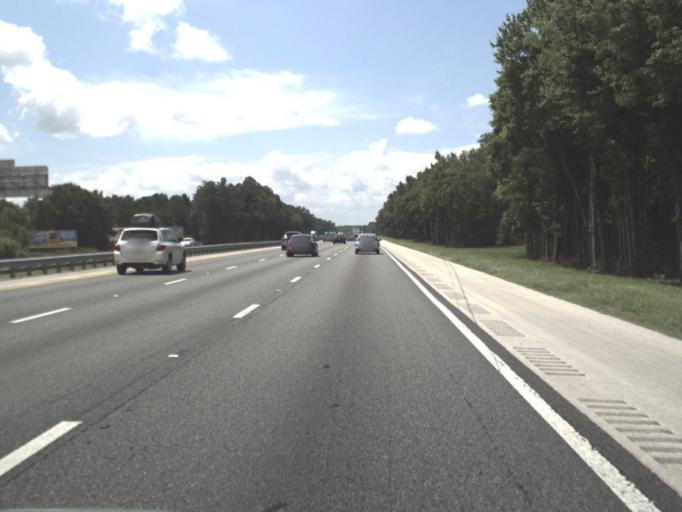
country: US
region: Florida
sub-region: Saint Johns County
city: Villano Beach
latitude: 29.9696
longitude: -81.4520
